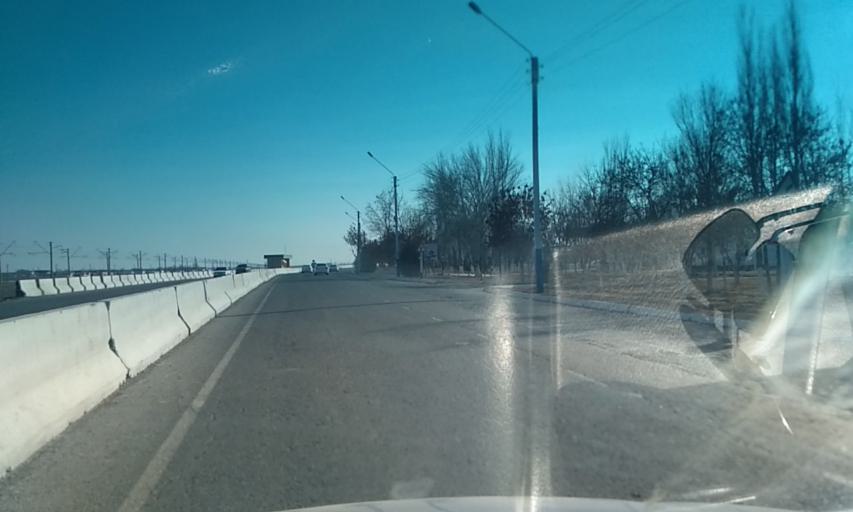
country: UZ
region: Sirdaryo
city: Guliston
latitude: 40.4708
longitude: 68.7717
